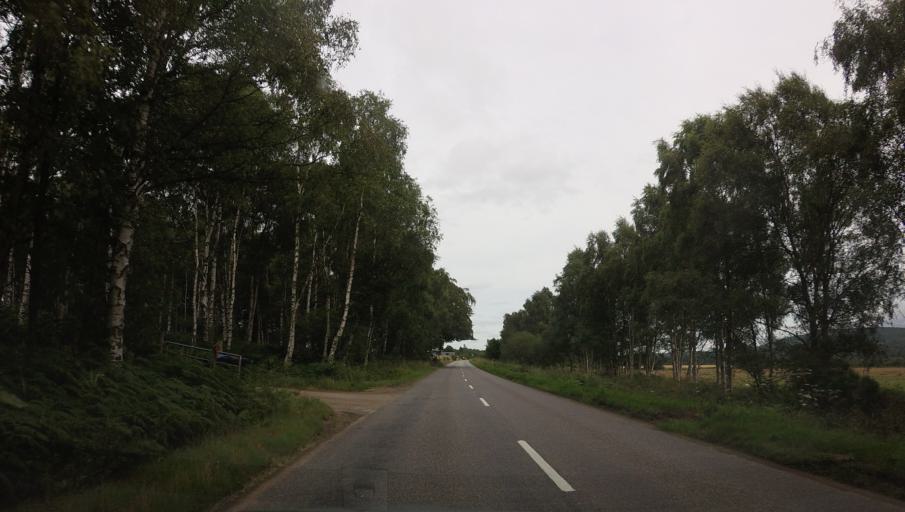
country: GB
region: Scotland
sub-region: Aberdeenshire
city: Aboyne
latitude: 57.0779
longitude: -2.8280
